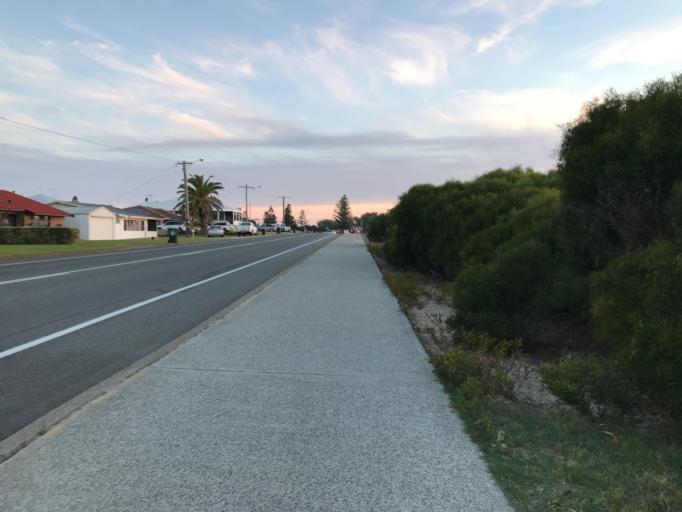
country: AU
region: Western Australia
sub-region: Rockingham
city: Shoalwater
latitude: -32.3021
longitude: 115.7033
